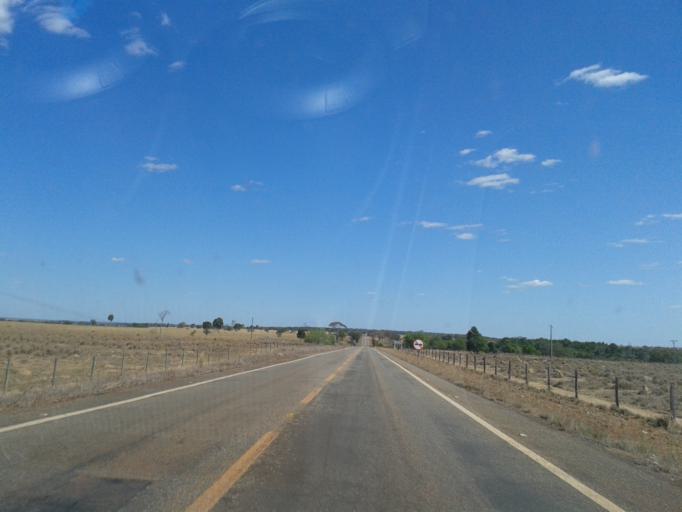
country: BR
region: Goias
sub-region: Sao Miguel Do Araguaia
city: Sao Miguel do Araguaia
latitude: -13.4346
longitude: -50.2840
